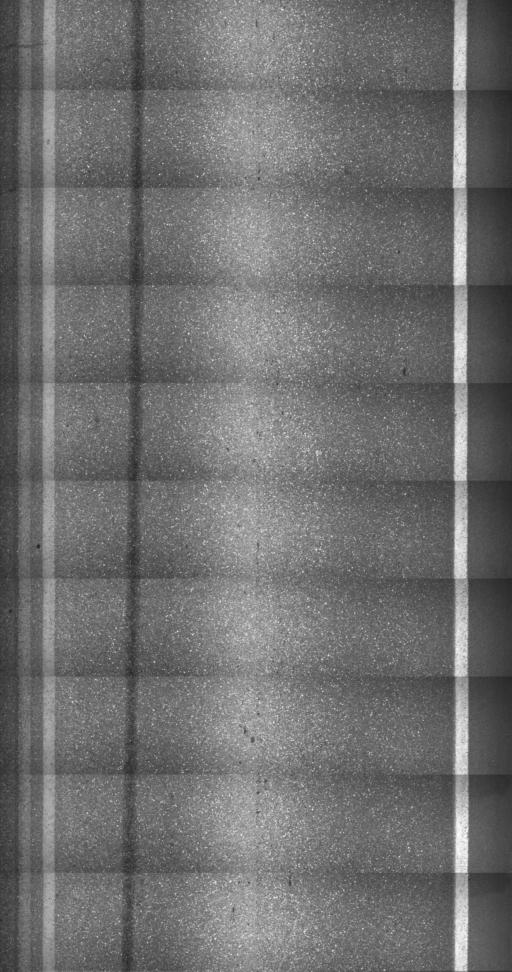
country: US
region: Vermont
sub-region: Chittenden County
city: Jericho
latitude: 44.5184
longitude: -72.9480
